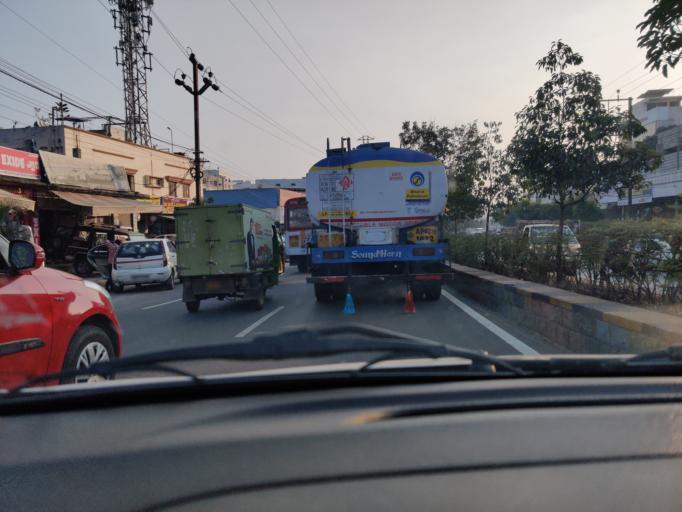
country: IN
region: Telangana
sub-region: Rangareddi
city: Uppal Kalan
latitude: 17.4321
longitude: 78.5543
